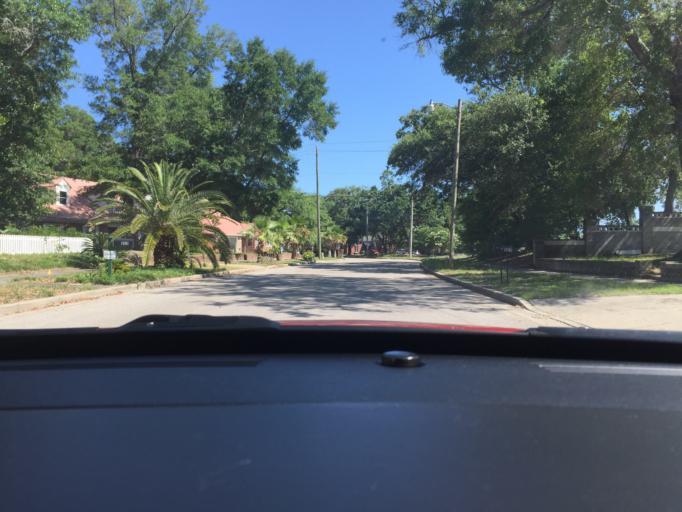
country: US
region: Mississippi
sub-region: Harrison County
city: Biloxi
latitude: 30.3927
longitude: -88.9876
